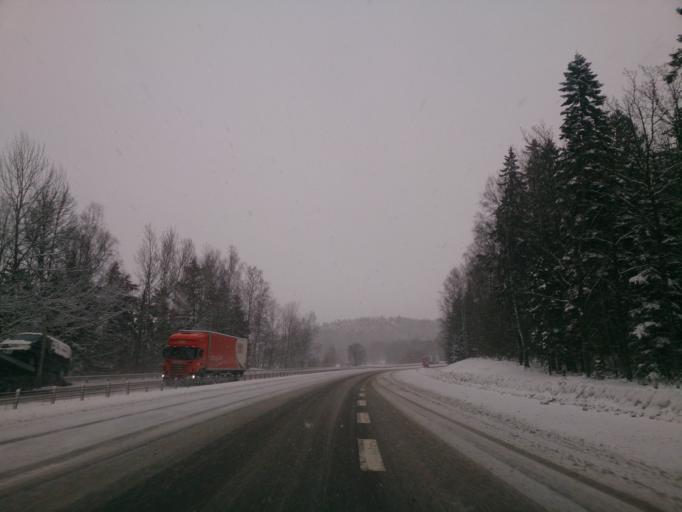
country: SE
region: Soedermanland
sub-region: Nykopings Kommun
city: Nykoping
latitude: 58.7661
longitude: 16.9933
